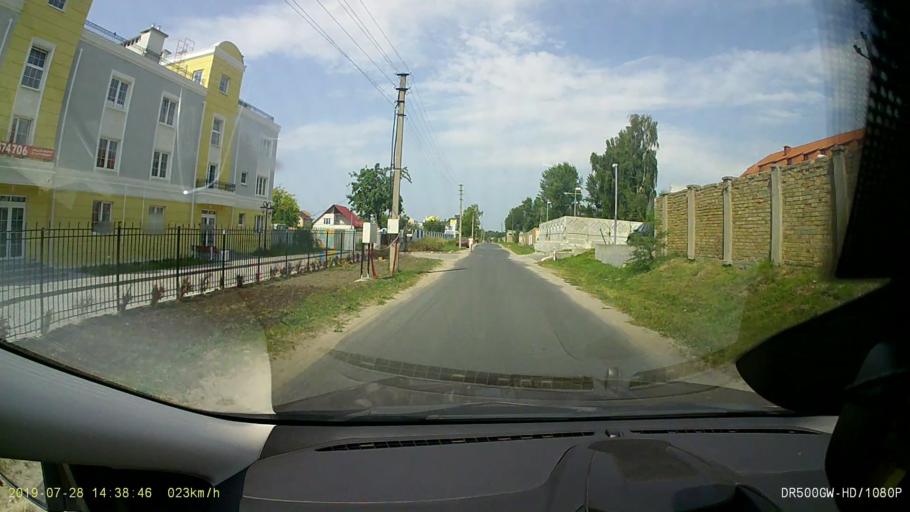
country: RU
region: Kaliningrad
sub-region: Gorod Kaliningrad
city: Yantarnyy
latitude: 54.8722
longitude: 19.9397
